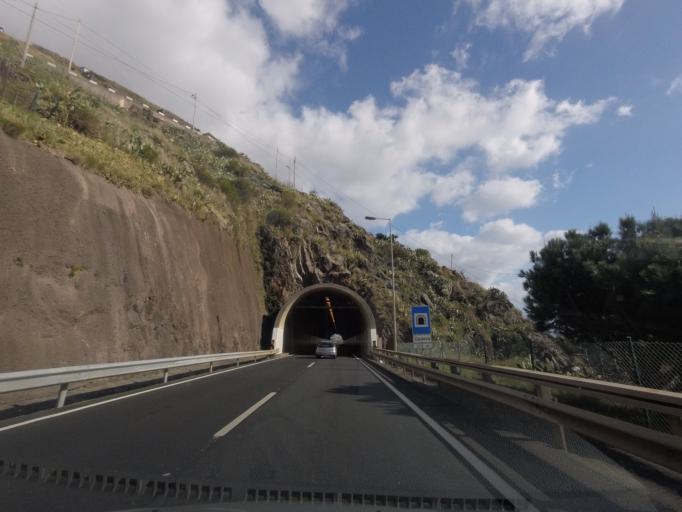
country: PT
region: Madeira
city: Camara de Lobos
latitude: 32.6601
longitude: -16.9951
